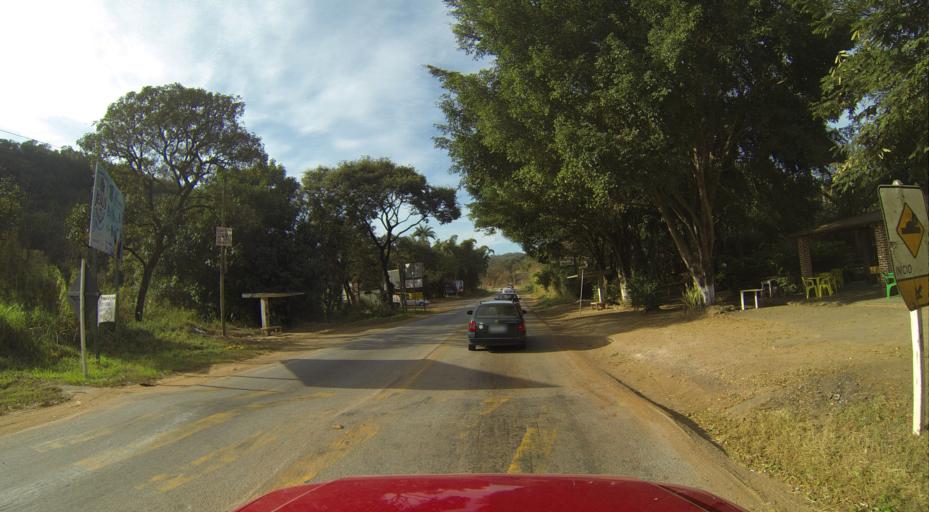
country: BR
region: Minas Gerais
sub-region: Brumadinho
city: Brumadinho
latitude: -20.0884
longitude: -44.2092
